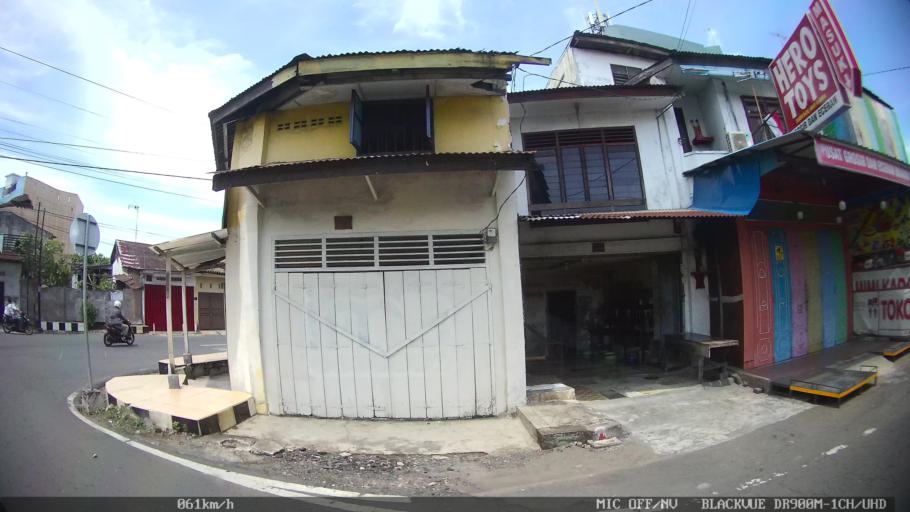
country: ID
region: North Sumatra
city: Binjai
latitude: 3.5994
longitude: 98.4897
